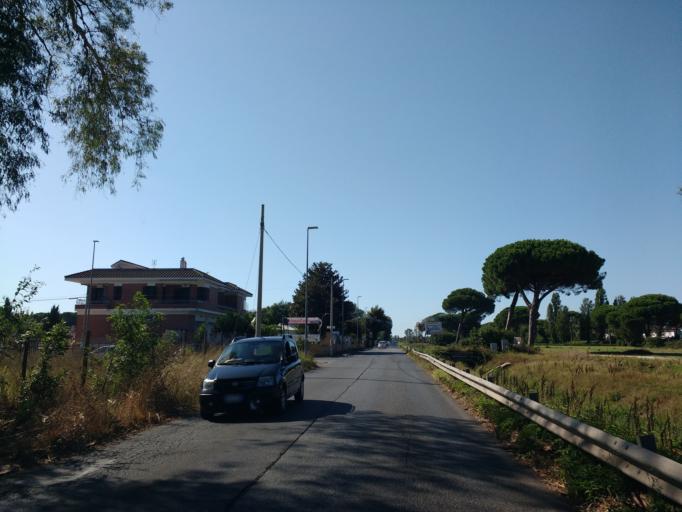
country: IT
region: Latium
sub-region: Citta metropolitana di Roma Capitale
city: Acilia-Castel Fusano-Ostia Antica
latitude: 41.7398
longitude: 12.3419
